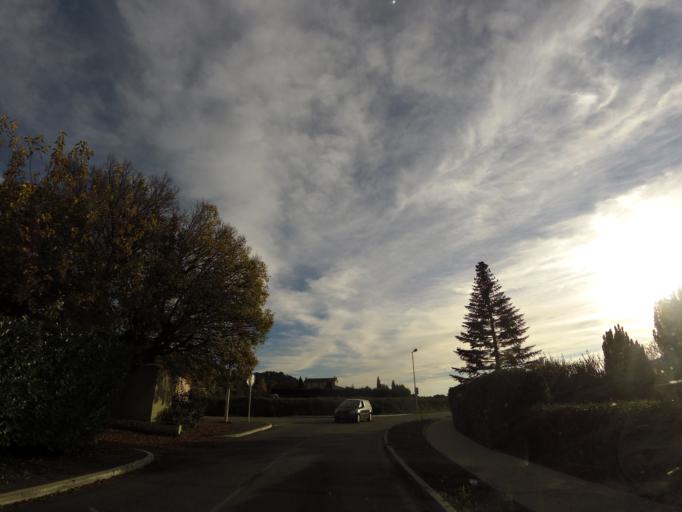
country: FR
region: Languedoc-Roussillon
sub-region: Departement du Gard
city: Ledignan
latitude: 44.0042
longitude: 4.1293
